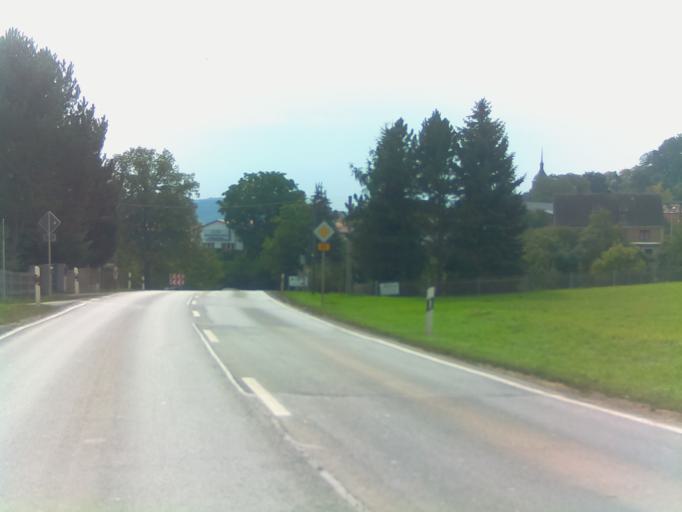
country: DE
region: Thuringia
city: Rothenstein
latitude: 50.8519
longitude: 11.6040
